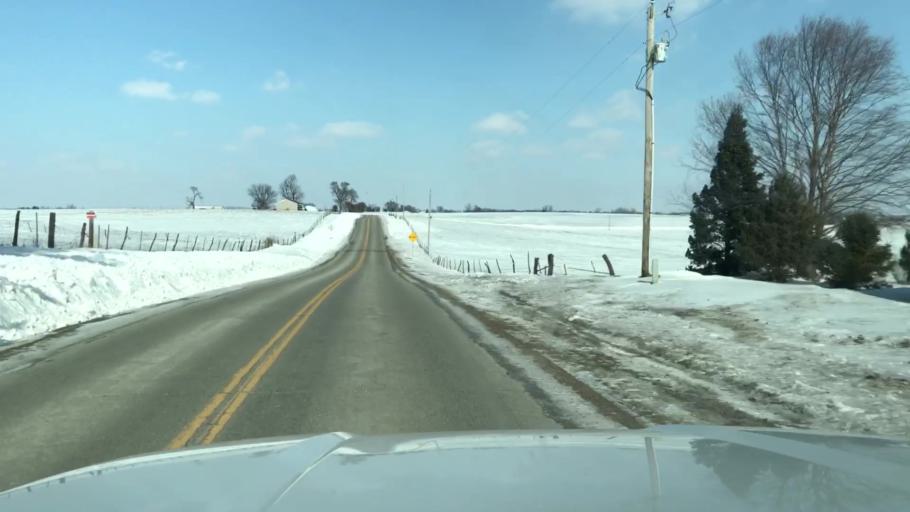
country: US
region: Missouri
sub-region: Nodaway County
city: Maryville
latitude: 40.3827
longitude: -94.7215
